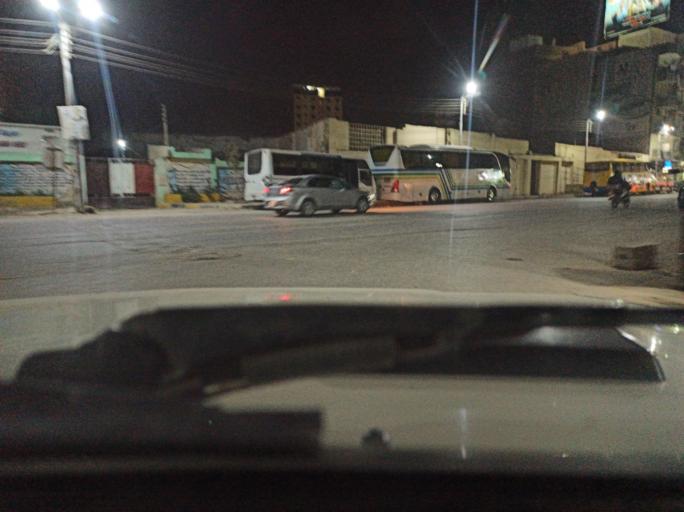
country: EG
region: Muhafazat Bani Suwayf
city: Bani Suwayf
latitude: 29.0765
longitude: 31.0875
